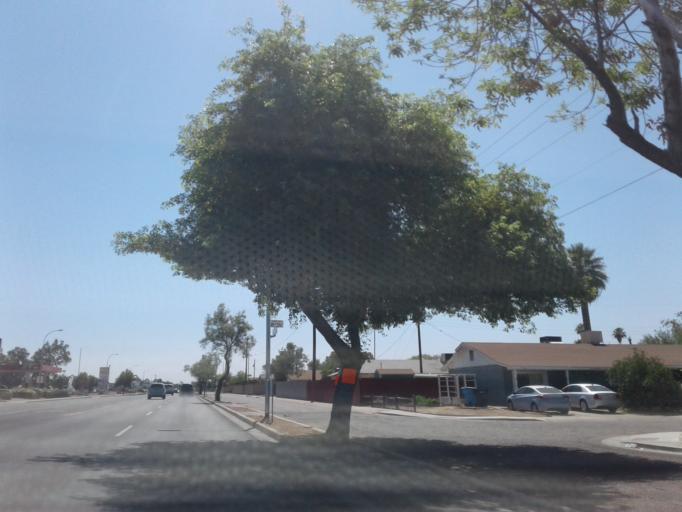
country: US
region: Arizona
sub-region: Maricopa County
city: Tolleson
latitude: 33.4944
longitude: -112.2282
